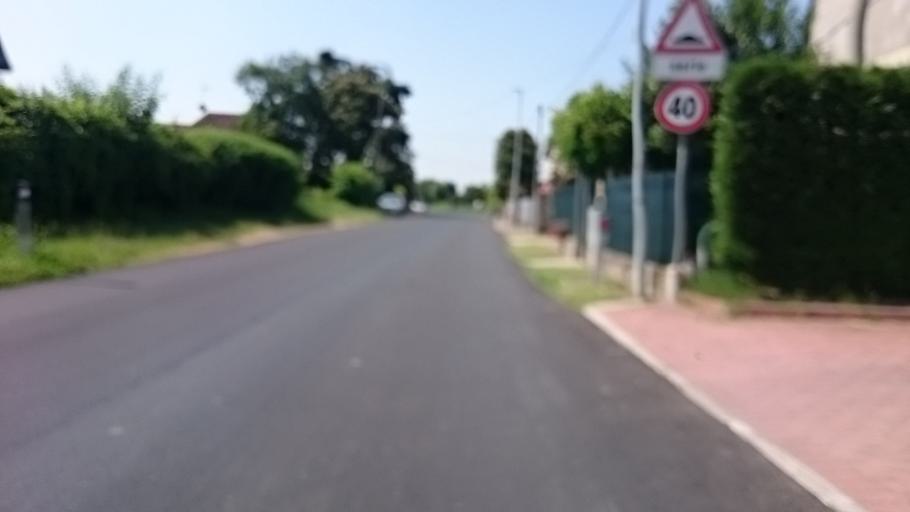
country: IT
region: Veneto
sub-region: Provincia di Padova
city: Albignasego
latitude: 45.3347
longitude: 11.8807
